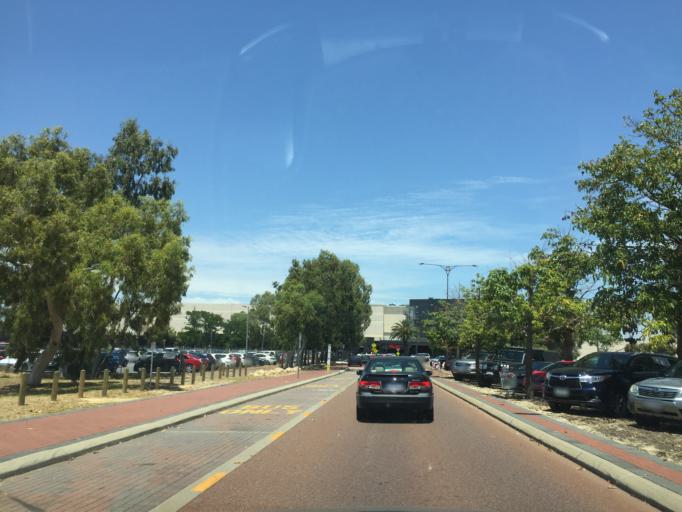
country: AU
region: Western Australia
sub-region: Canning
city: Cannington
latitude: -32.0184
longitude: 115.9403
